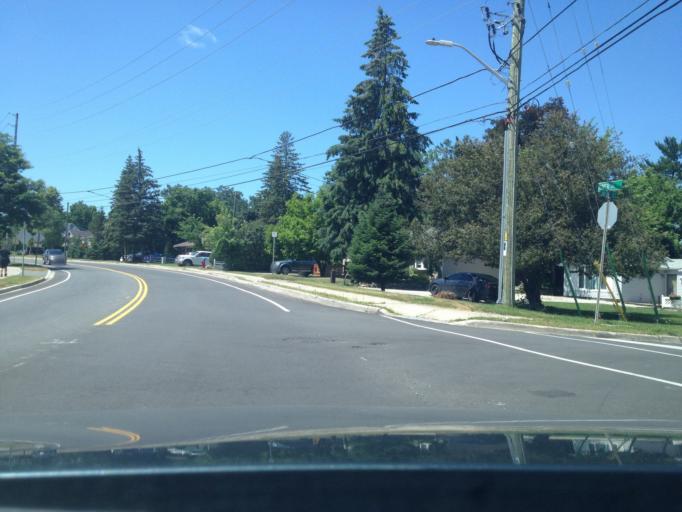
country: CA
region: Ontario
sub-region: Halton
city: Milton
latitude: 43.6603
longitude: -79.9127
